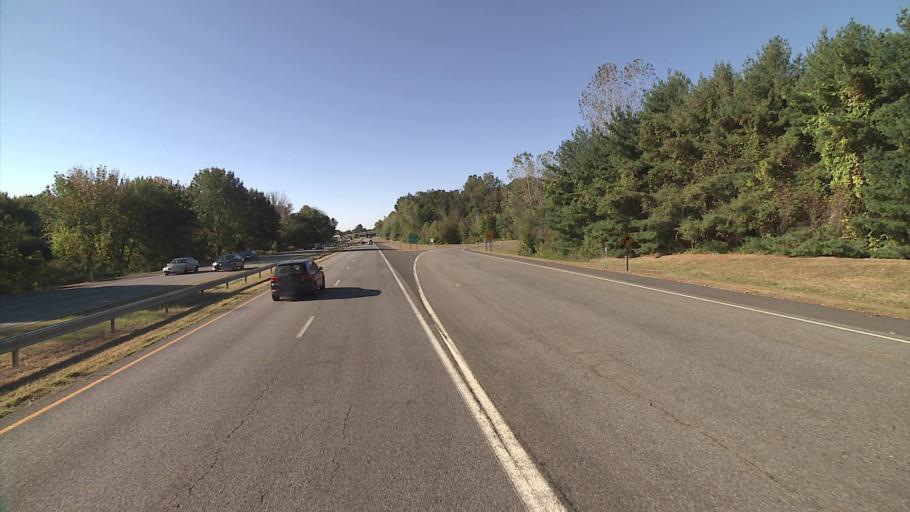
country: US
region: Connecticut
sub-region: New Haven County
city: Wallingford
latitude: 41.4668
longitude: -72.8309
